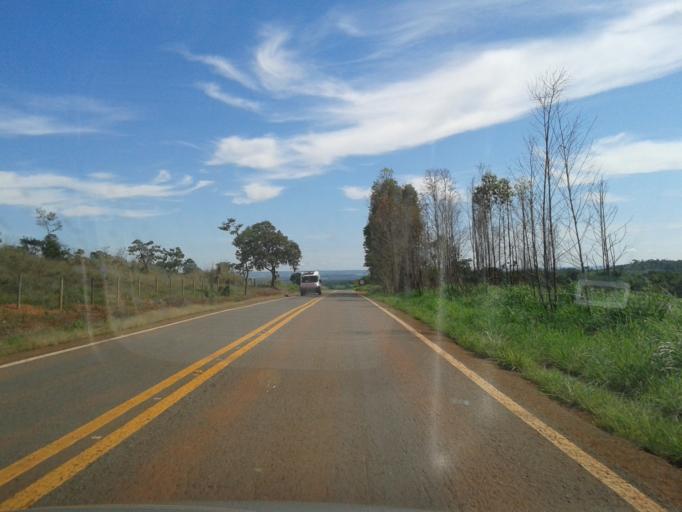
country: BR
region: Goias
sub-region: Piracanjuba
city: Piracanjuba
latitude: -17.2399
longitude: -48.7365
